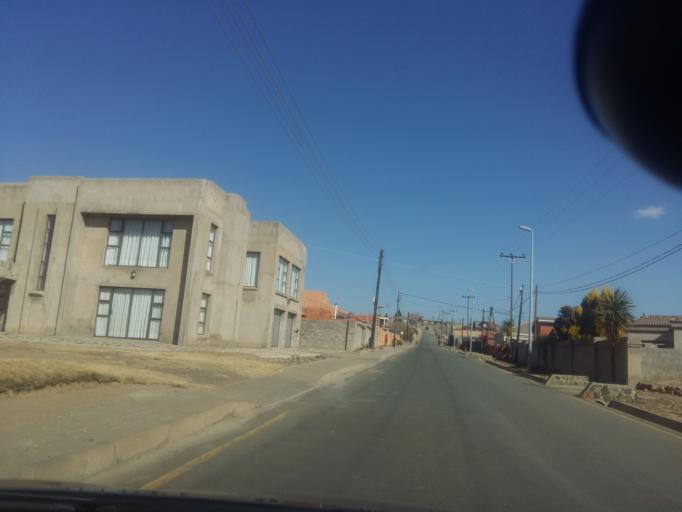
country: LS
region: Maseru
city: Maseru
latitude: -29.3461
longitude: 27.4522
